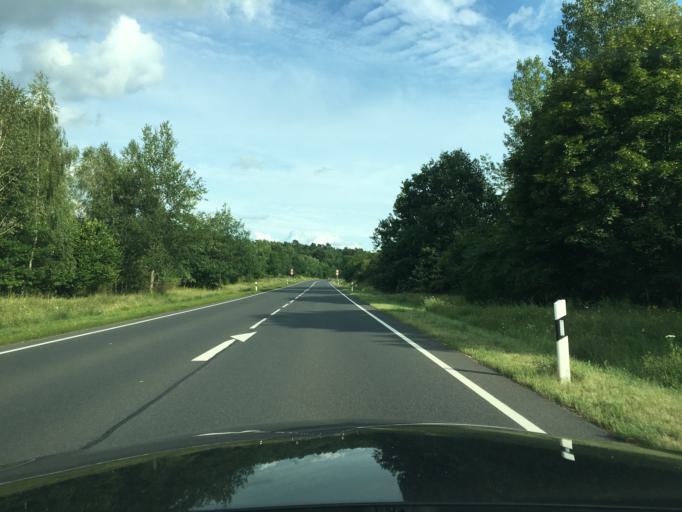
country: DE
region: Mecklenburg-Vorpommern
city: Neustrelitz
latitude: 53.3783
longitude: 13.0655
